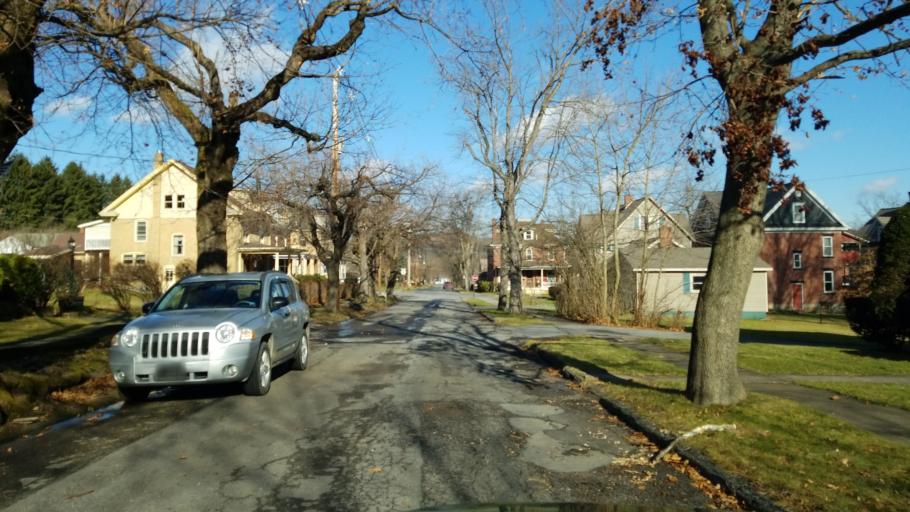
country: US
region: Pennsylvania
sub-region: Clearfield County
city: Clearfield
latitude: 41.0213
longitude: -78.4469
